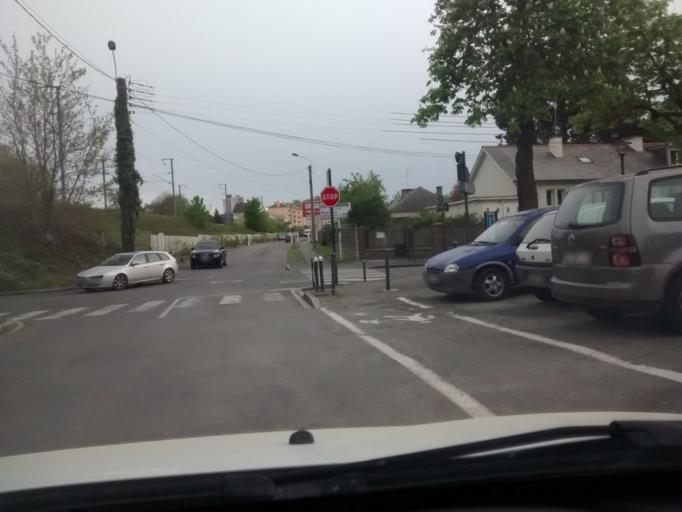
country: FR
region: Brittany
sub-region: Departement d'Ille-et-Vilaine
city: Rennes
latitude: 48.1231
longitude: -1.6887
